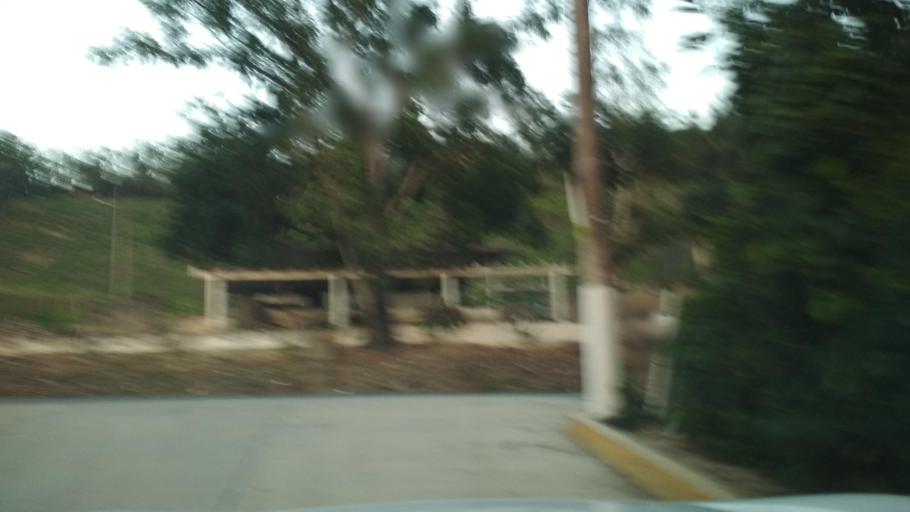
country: MX
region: Veracruz
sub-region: Poza Rica de Hidalgo
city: Arroyo del Maiz Uno
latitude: 20.4783
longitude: -97.3857
